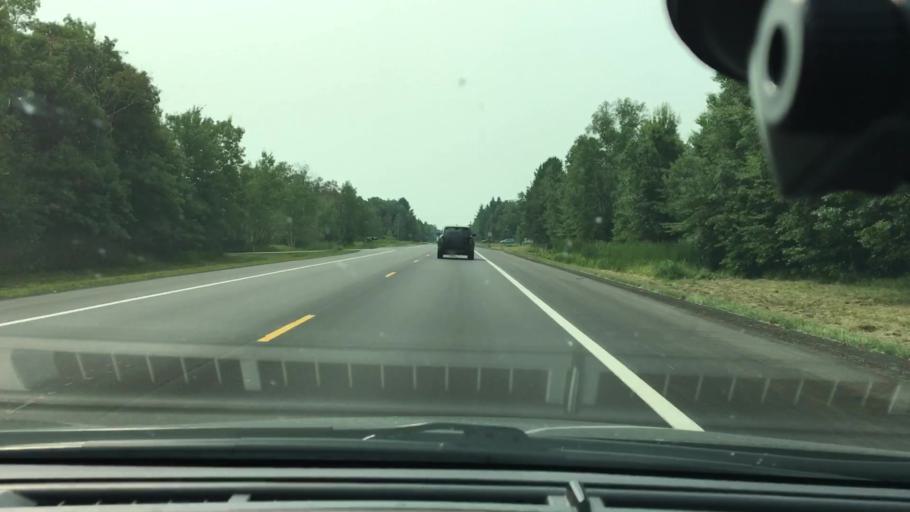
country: US
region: Minnesota
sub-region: Crow Wing County
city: Brainerd
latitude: 46.4527
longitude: -94.1722
